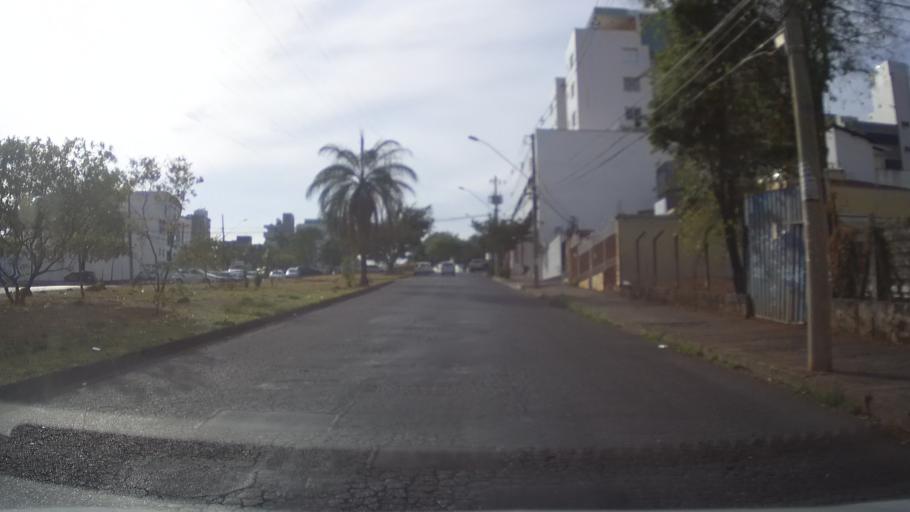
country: BR
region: Minas Gerais
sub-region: Contagem
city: Contagem
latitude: -19.8815
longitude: -44.0009
